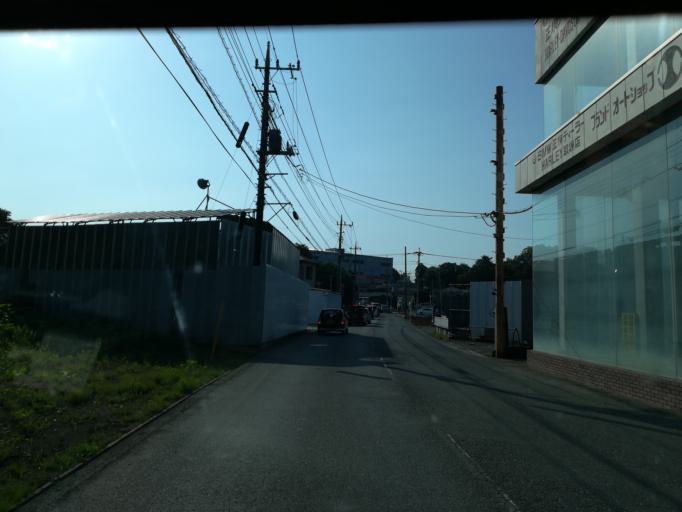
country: JP
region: Saitama
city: Sayama
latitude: 35.8048
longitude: 139.3814
